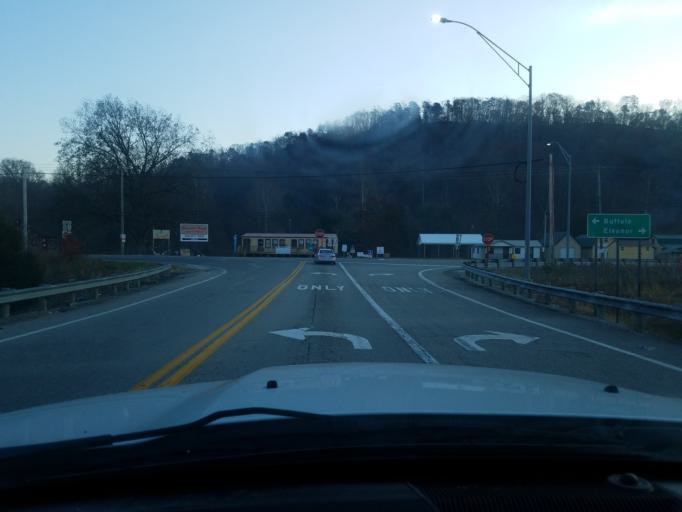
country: US
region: West Virginia
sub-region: Putnam County
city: Buffalo
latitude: 38.5833
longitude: -81.9950
